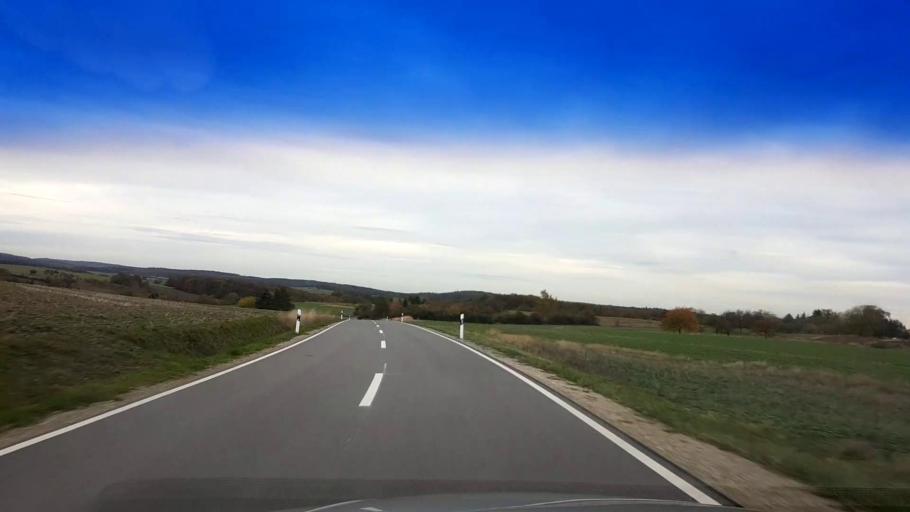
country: DE
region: Bavaria
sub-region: Upper Franconia
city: Priesendorf
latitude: 49.9279
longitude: 10.7050
